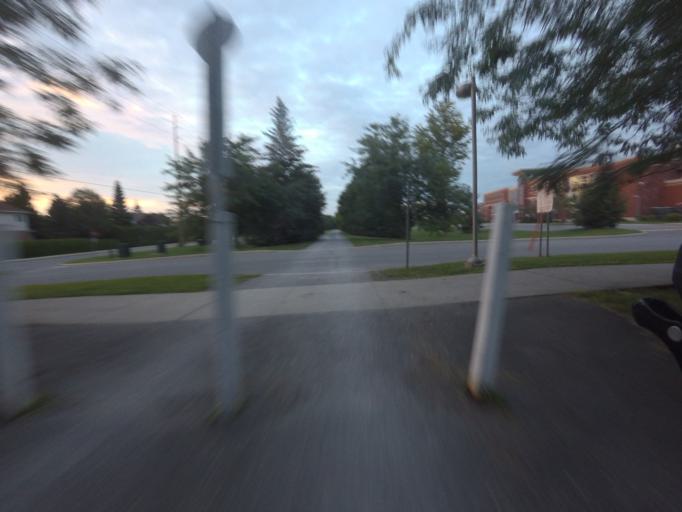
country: CA
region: Ontario
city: Bells Corners
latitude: 45.2638
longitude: -75.9119
